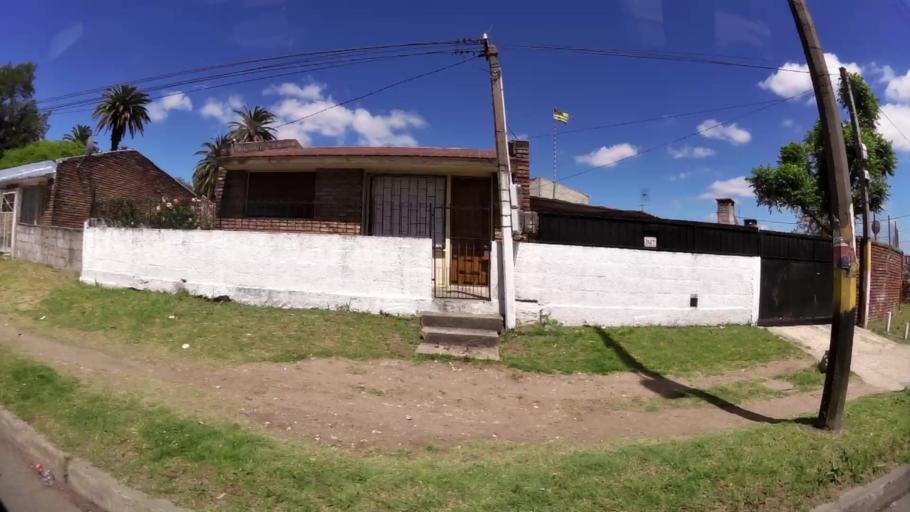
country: UY
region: Montevideo
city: Montevideo
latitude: -34.8491
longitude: -56.1334
